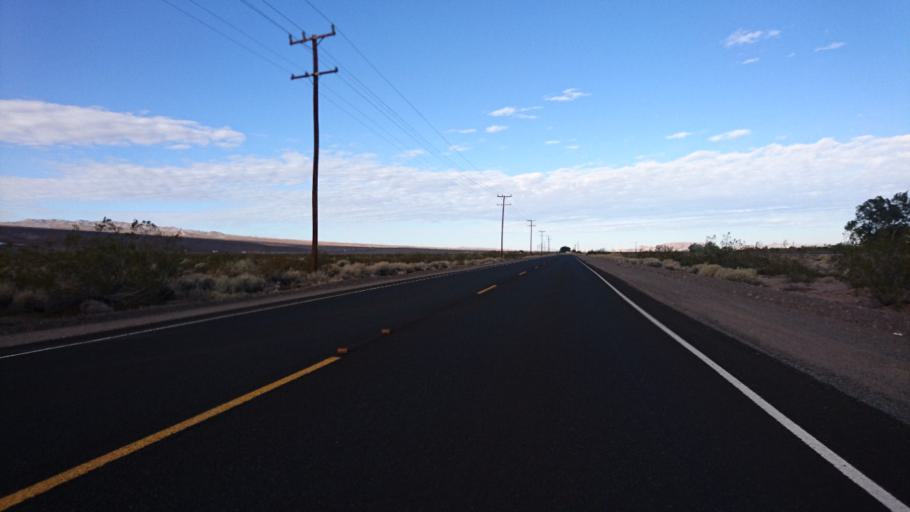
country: US
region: California
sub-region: San Bernardino County
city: Barstow
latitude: 34.8435
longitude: -116.7615
